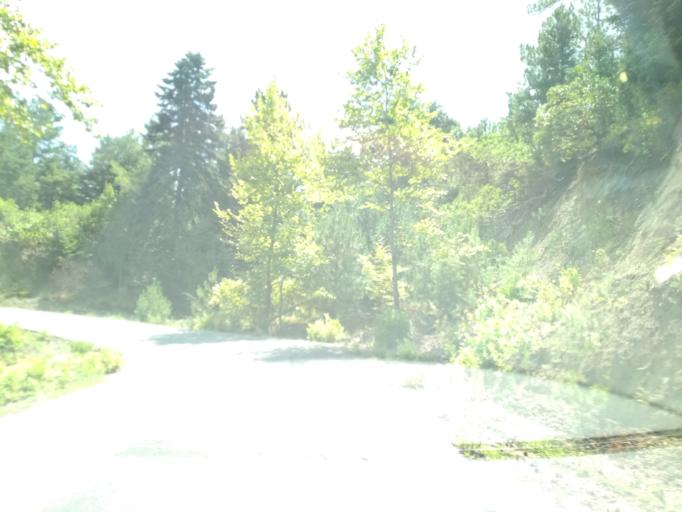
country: GR
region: Central Greece
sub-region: Nomos Evvoias
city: Roviai
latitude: 38.8614
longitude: 23.2851
